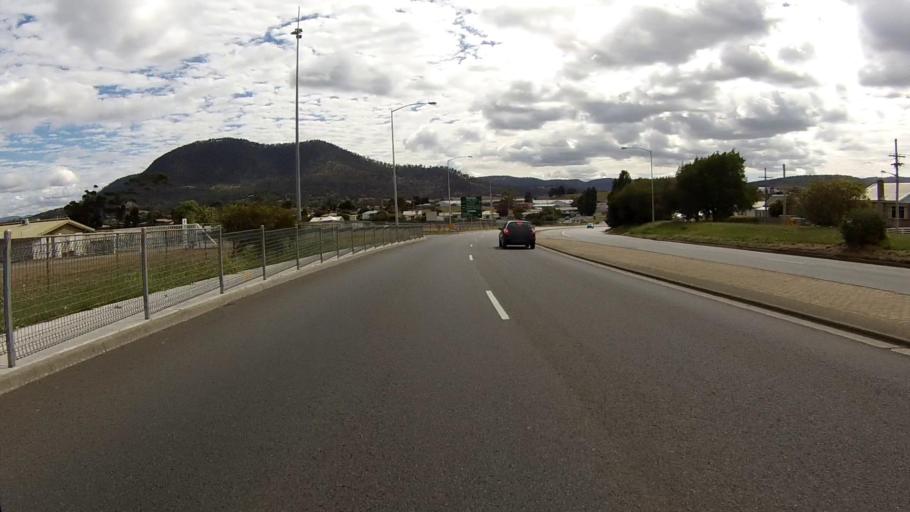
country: AU
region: Tasmania
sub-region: Glenorchy
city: Goodwood
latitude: -42.8245
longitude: 147.2910
